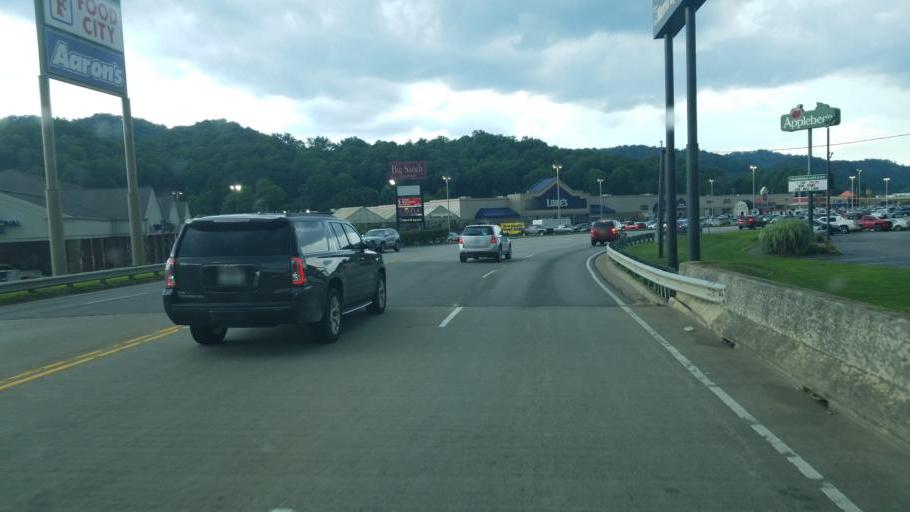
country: US
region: Kentucky
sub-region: Pike County
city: Coal Run Village
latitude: 37.5037
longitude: -82.5338
